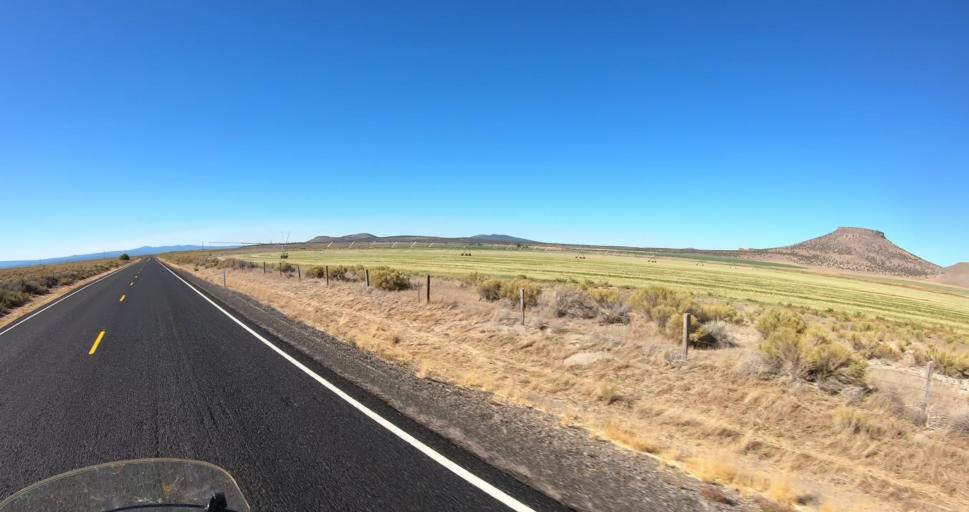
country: US
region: Oregon
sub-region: Deschutes County
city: La Pine
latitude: 43.1282
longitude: -120.8953
